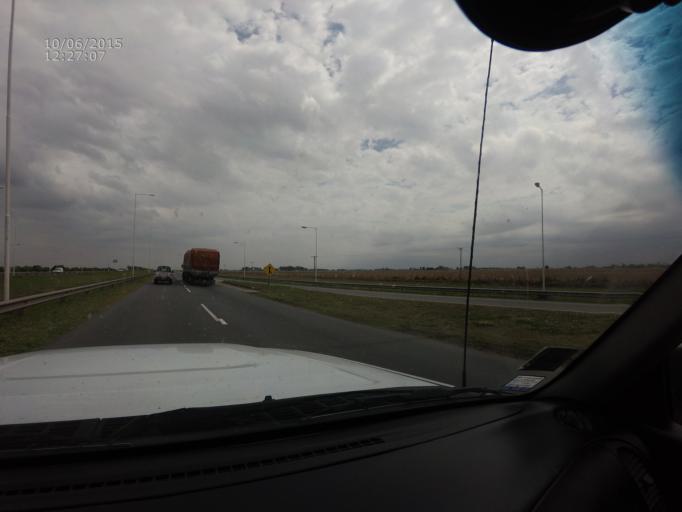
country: AR
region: Santa Fe
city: Roldan
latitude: -32.9008
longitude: -61.0329
